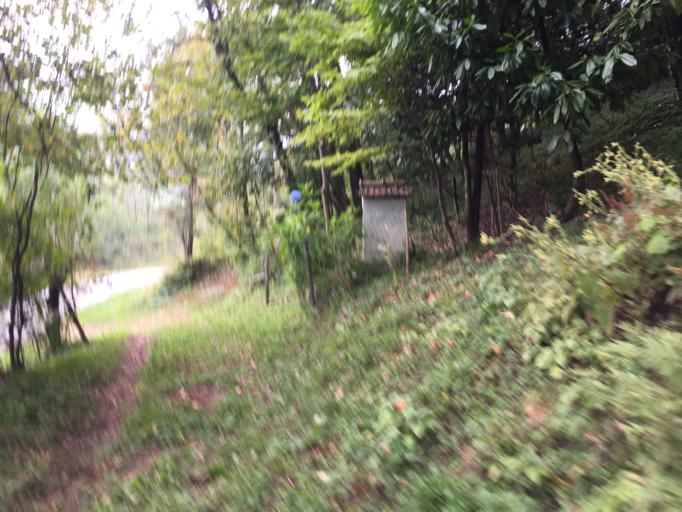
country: IT
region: Piedmont
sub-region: Provincia di Cuneo
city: Chiusa di Pesio
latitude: 44.3193
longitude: 7.6948
